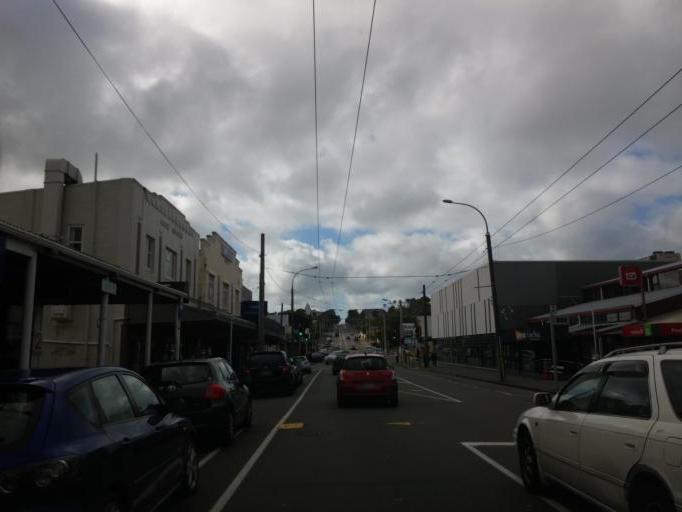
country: NZ
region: Wellington
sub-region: Wellington City
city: Kelburn
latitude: -41.2849
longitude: 174.7367
